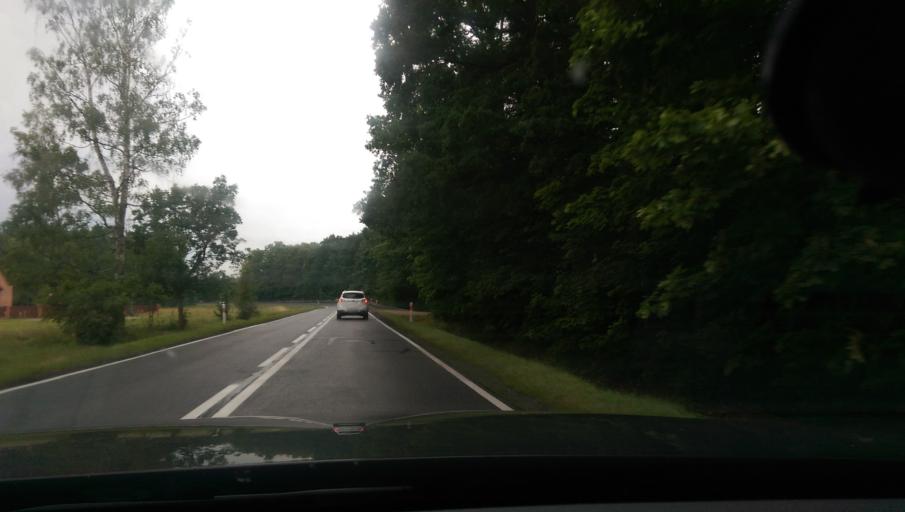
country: PL
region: Warmian-Masurian Voivodeship
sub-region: Powiat szczycienski
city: Szczytno
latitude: 53.5387
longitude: 20.9860
